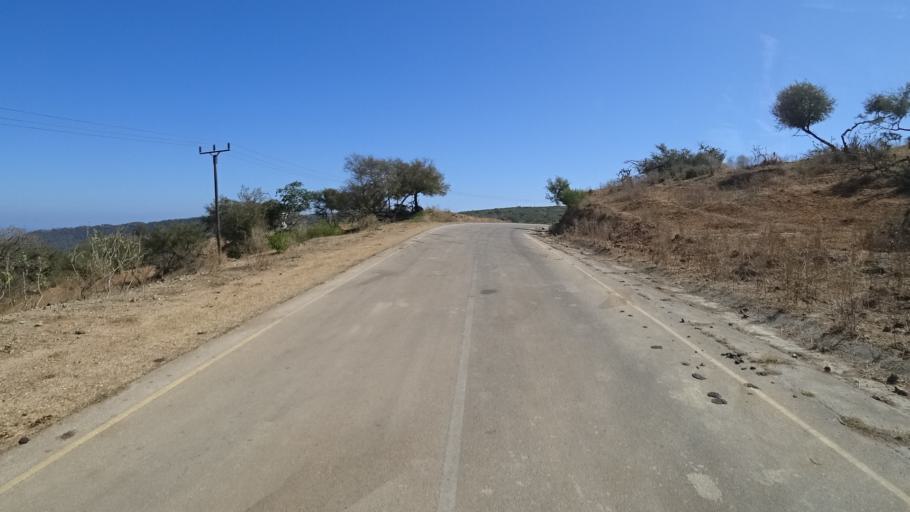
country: YE
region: Al Mahrah
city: Hawf
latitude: 16.7565
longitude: 53.3403
